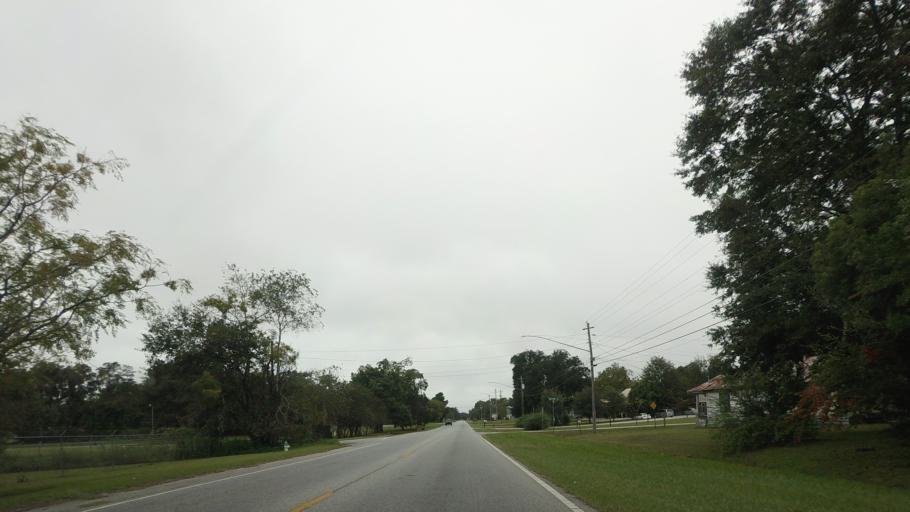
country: US
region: Georgia
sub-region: Lowndes County
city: Valdosta
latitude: 30.8181
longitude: -83.2622
